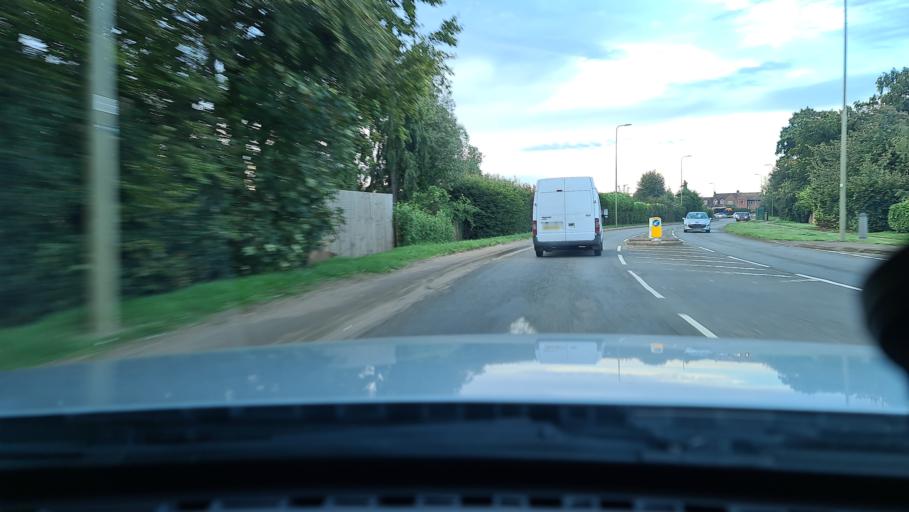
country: GB
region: England
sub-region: Oxfordshire
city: Banbury
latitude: 52.0701
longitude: -1.3617
